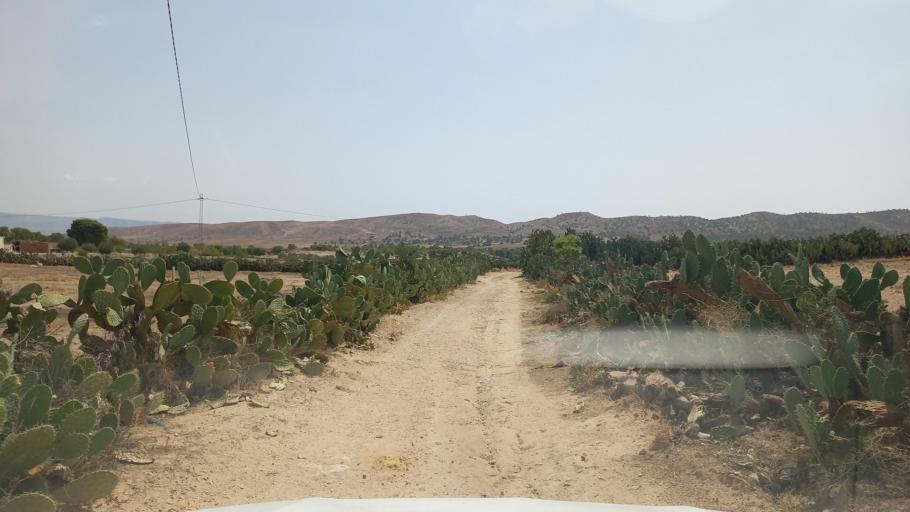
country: TN
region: Al Qasrayn
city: Sbiba
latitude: 35.3978
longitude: 8.9829
